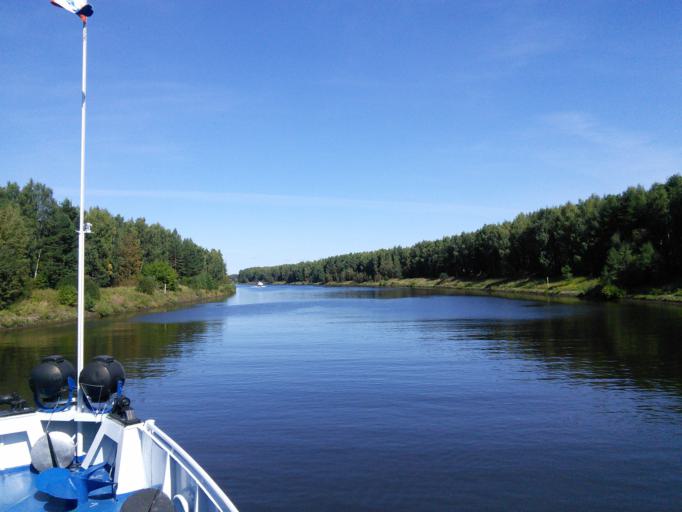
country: RU
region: Moskovskaya
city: Pirogovskiy
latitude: 56.0292
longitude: 37.6647
